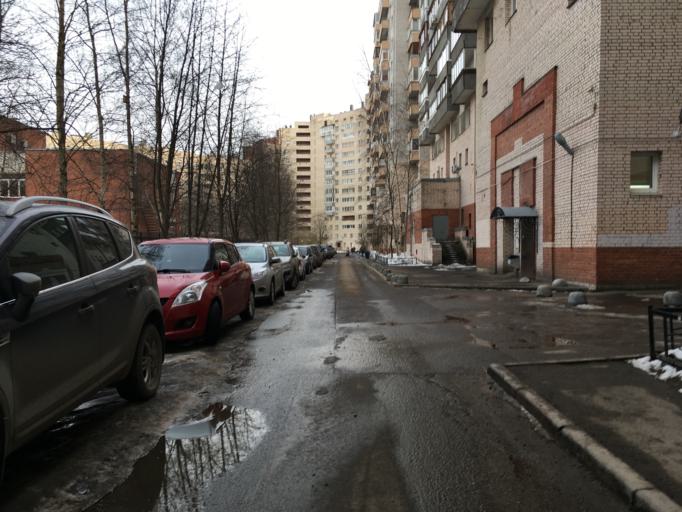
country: RU
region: St.-Petersburg
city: Komendantsky aerodrom
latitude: 60.0165
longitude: 30.2512
